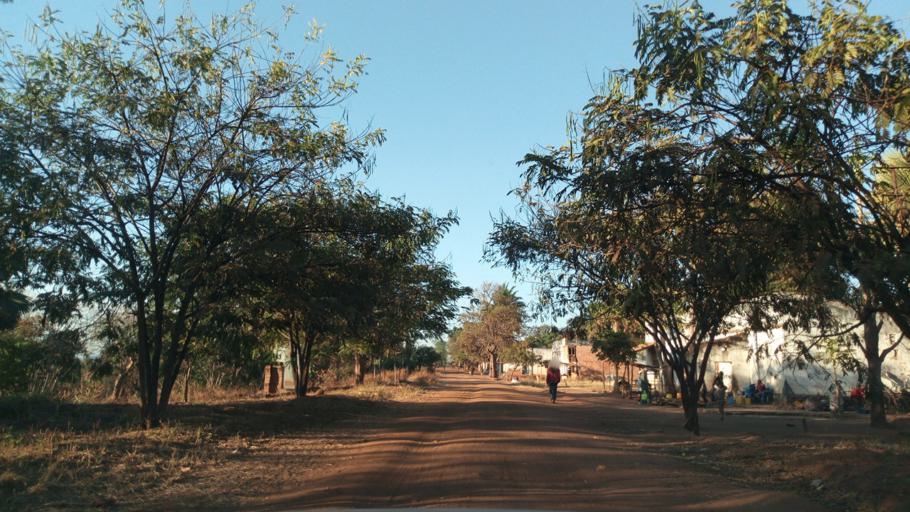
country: ZM
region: Luapula
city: Mwense
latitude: -10.3665
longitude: 28.6153
